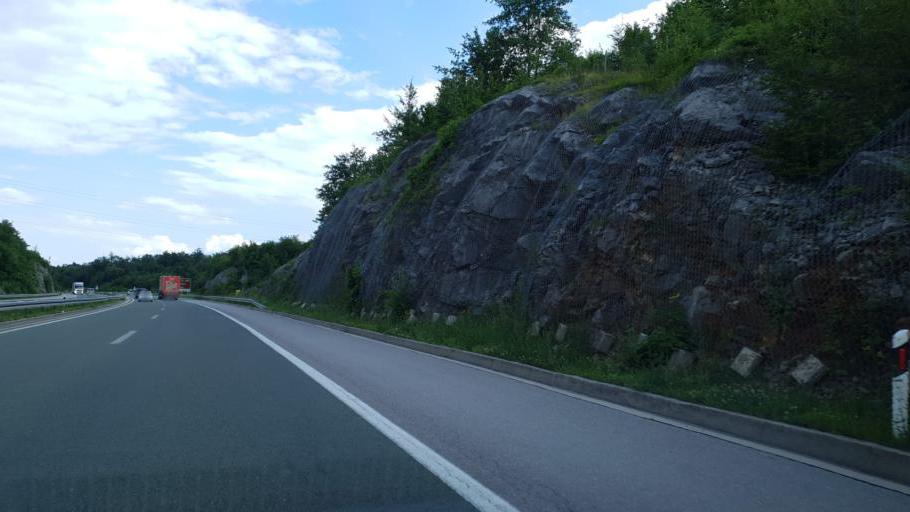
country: HR
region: Primorsko-Goranska
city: Matulji
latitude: 45.3843
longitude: 14.3029
